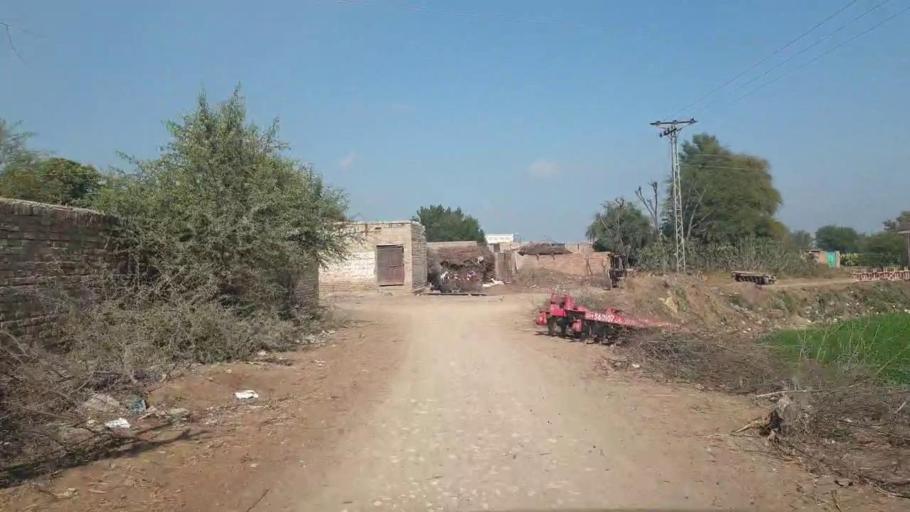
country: PK
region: Sindh
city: Shahdadpur
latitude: 25.9316
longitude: 68.5859
